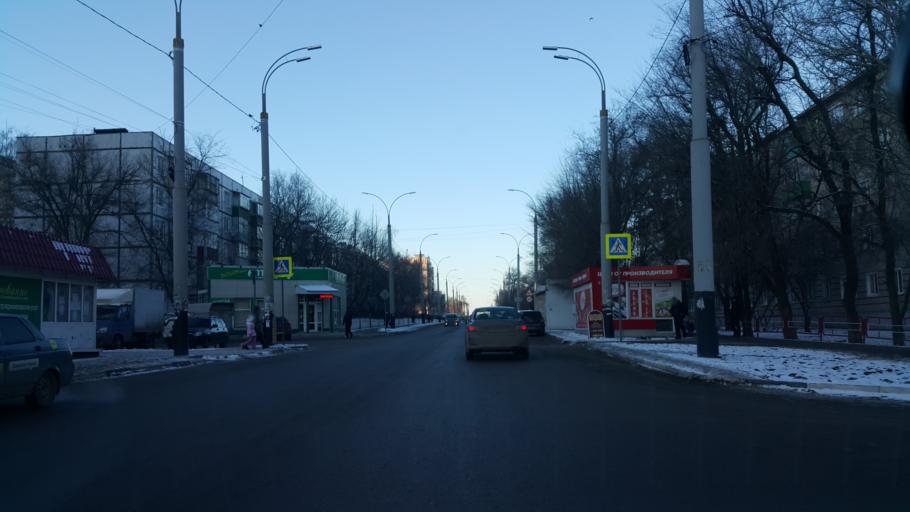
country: RU
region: Tambov
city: Pokrovo-Prigorodnoye
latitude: 52.7049
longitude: 41.3992
